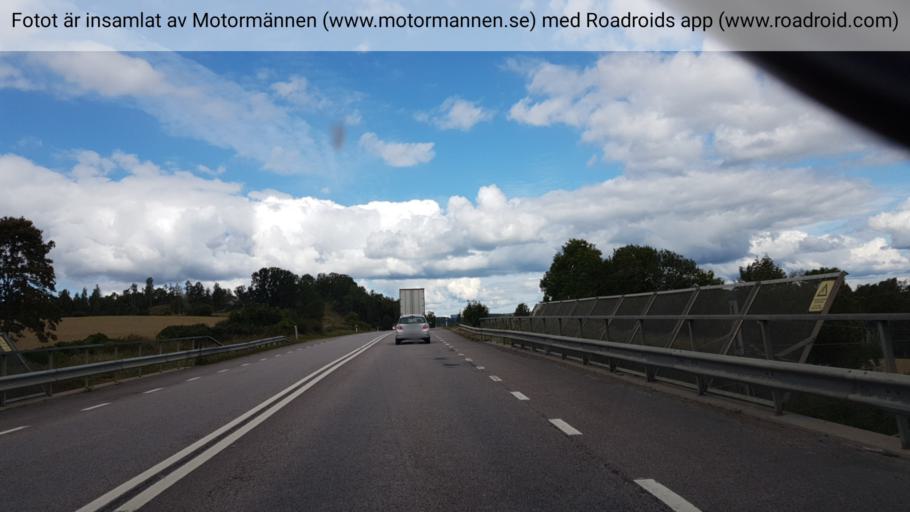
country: SE
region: Joenkoeping
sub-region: Tranas Kommun
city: Tranas
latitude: 57.9958
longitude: 14.9202
